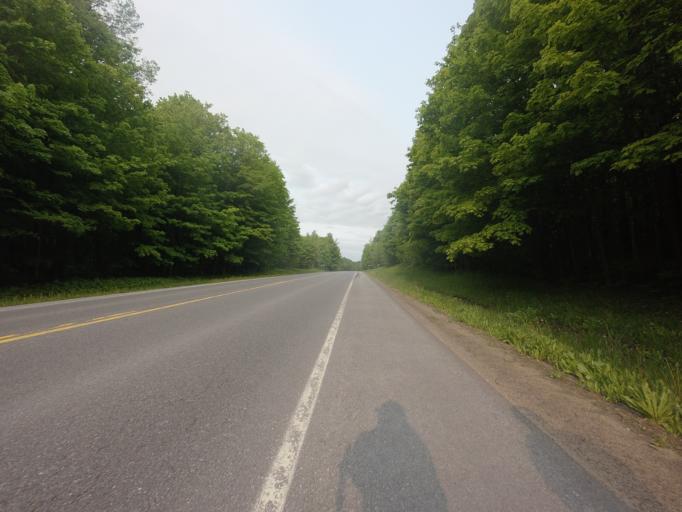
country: US
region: New York
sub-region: Jefferson County
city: Carthage
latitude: 44.0332
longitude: -75.5957
